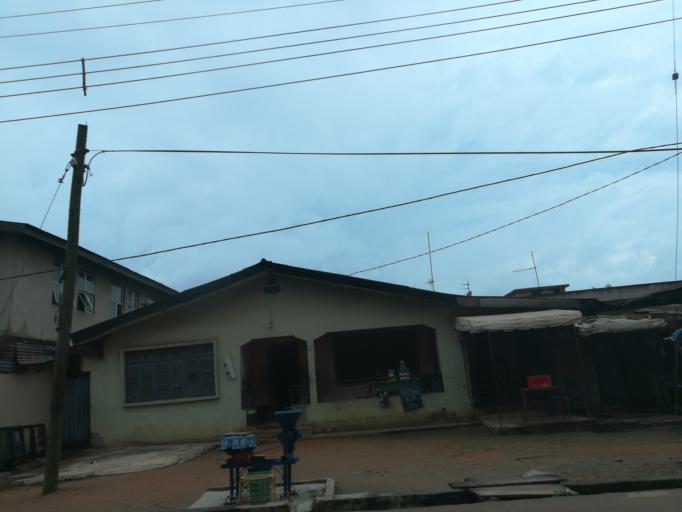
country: NG
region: Lagos
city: Agege
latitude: 6.6095
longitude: 3.3290
